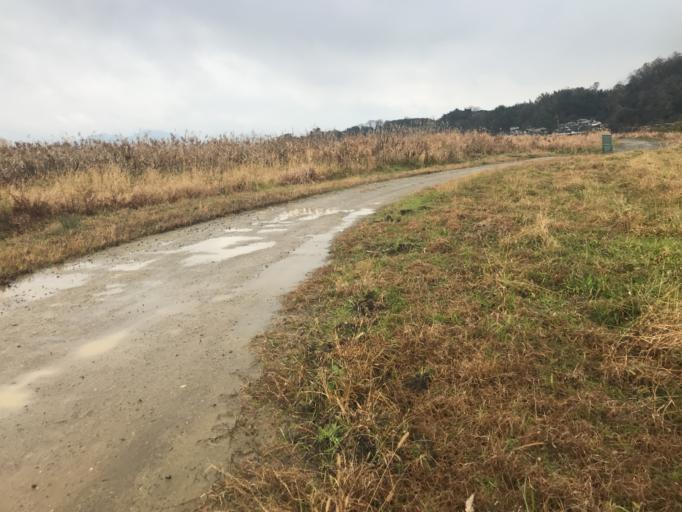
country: JP
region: Kyoto
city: Kameoka
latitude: 35.0159
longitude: 135.6011
